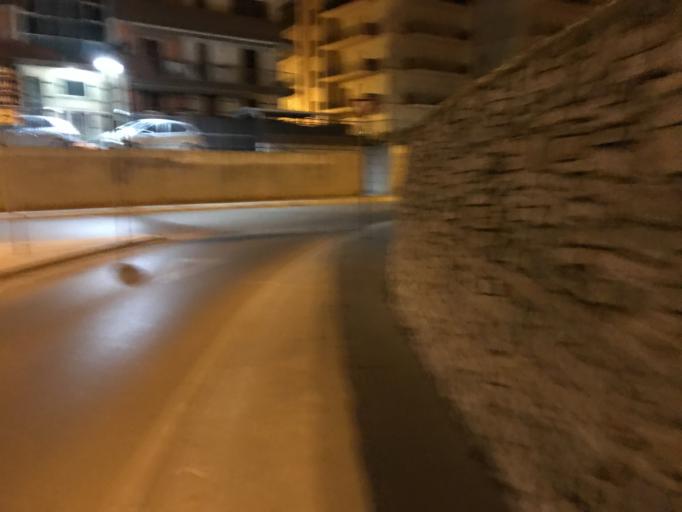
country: IT
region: Apulia
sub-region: Provincia di Bari
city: Corato
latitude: 41.1533
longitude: 16.4020
